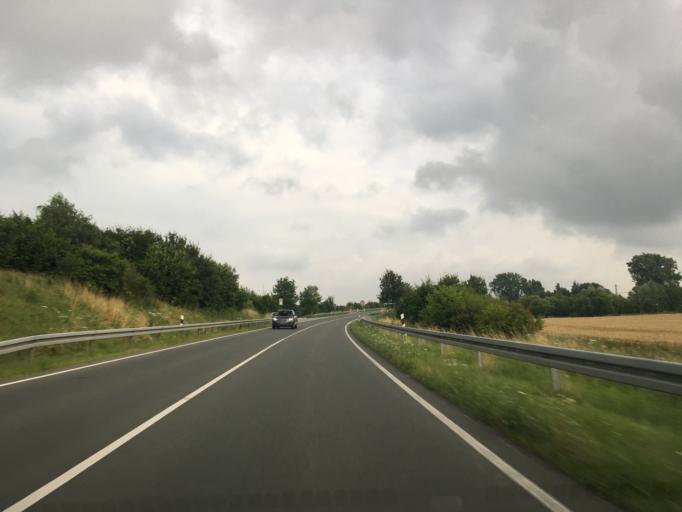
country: DE
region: North Rhine-Westphalia
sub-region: Regierungsbezirk Munster
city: Greven
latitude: 52.0420
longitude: 7.6225
